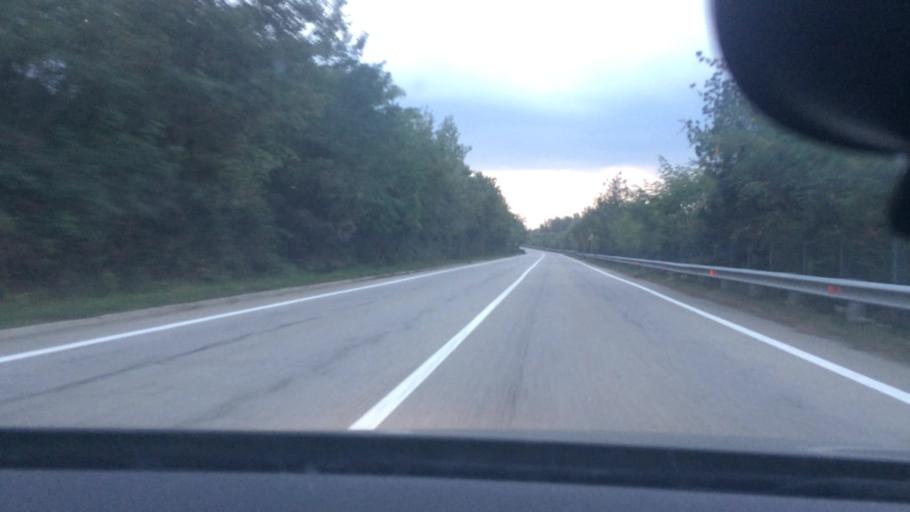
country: IT
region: Lombardy
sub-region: Provincia di Varese
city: Vizzola Ticino
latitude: 45.6247
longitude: 8.7065
